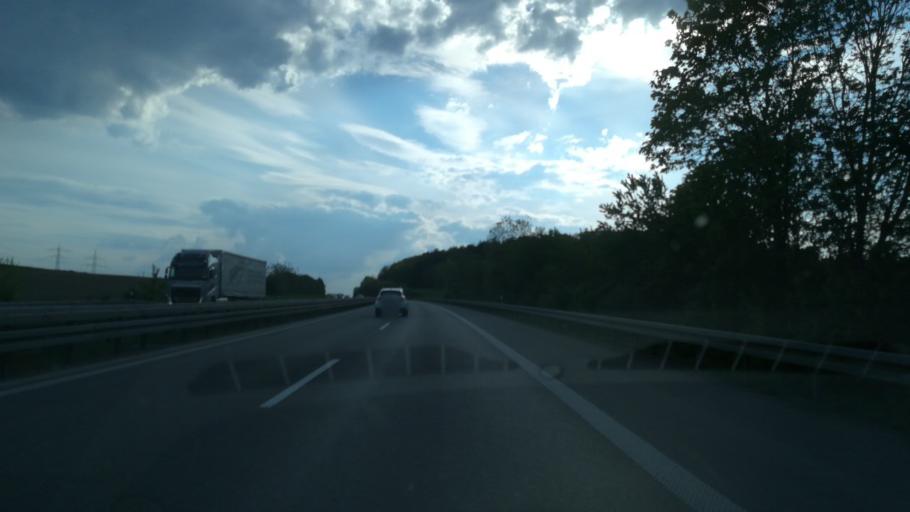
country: DE
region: Baden-Wuerttemberg
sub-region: Freiburg Region
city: Steisslingen
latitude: 47.8281
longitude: 8.9247
